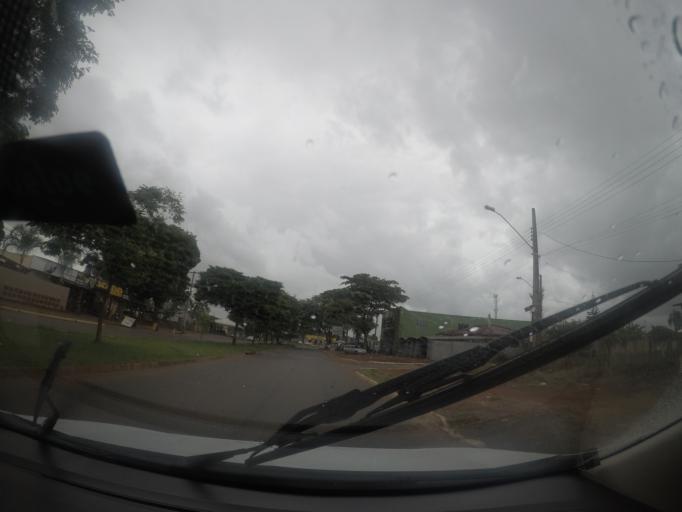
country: BR
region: Goias
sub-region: Trindade
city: Trindade
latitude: -16.6483
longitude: -49.3884
